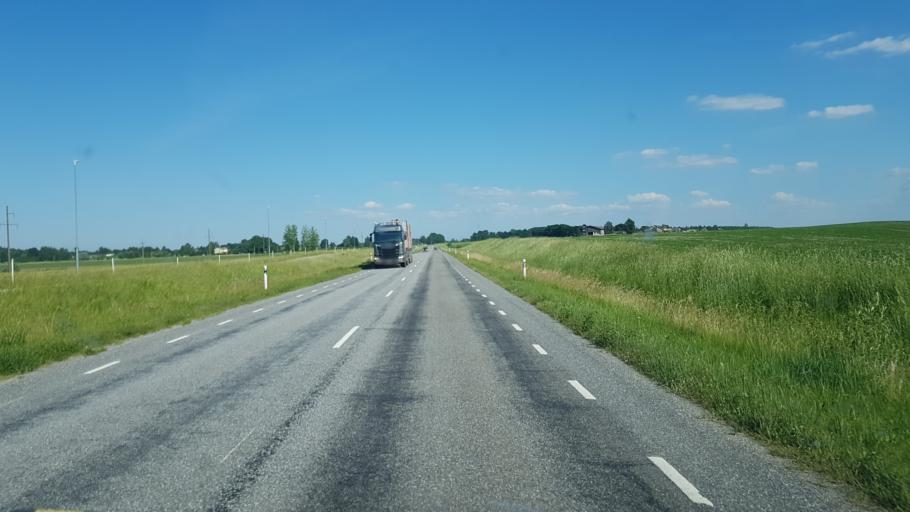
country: EE
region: Vorumaa
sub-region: Voru linn
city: Voru
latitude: 57.8579
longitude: 27.1488
